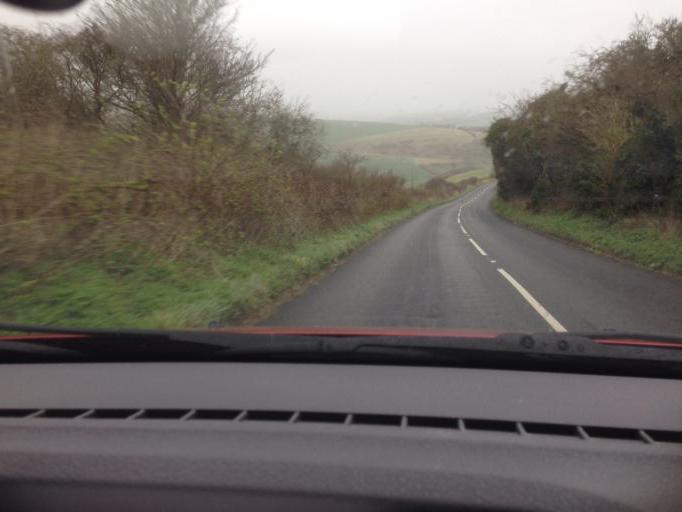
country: GB
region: England
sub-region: East Sussex
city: Seaford
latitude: 50.7904
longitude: 0.1402
